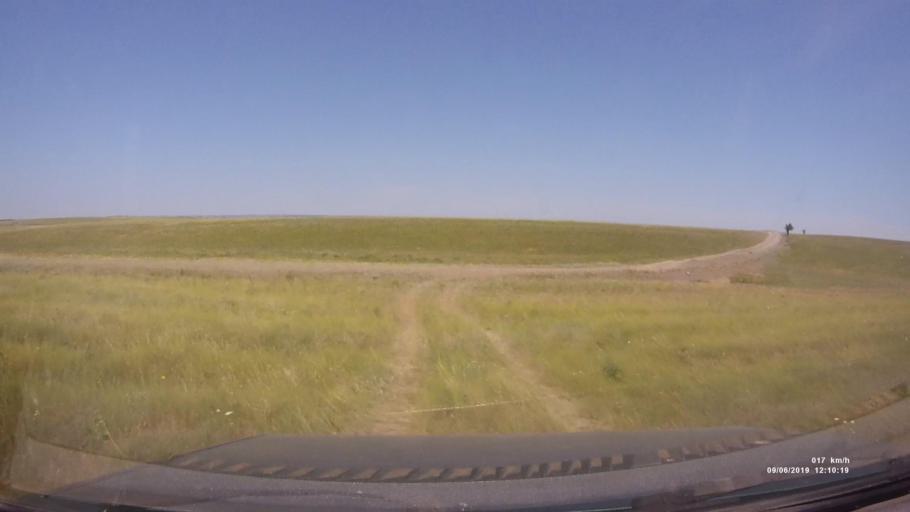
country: RU
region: Rostov
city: Staraya Stanitsa
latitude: 48.2500
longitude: 40.3389
